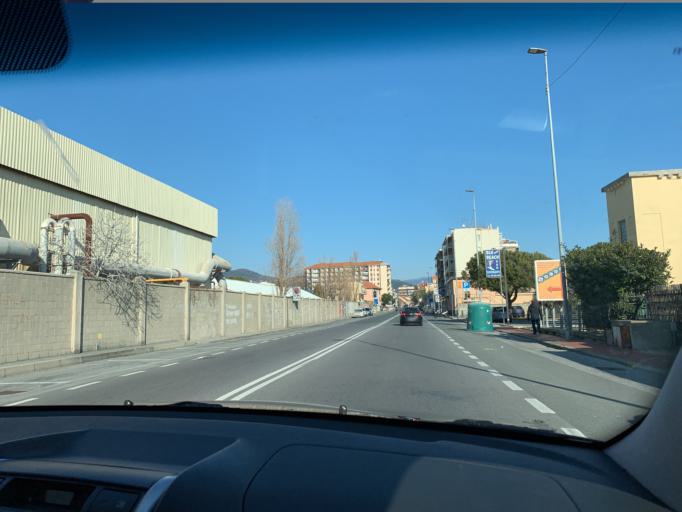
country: IT
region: Liguria
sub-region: Provincia di Savona
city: Valleggia
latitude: 44.2790
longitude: 8.4423
